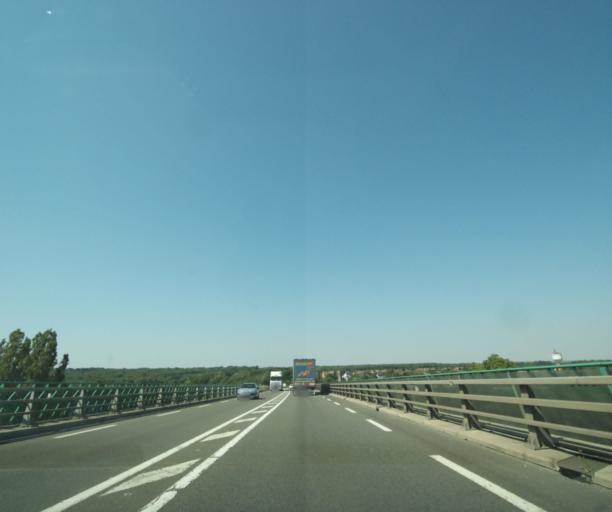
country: FR
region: Lorraine
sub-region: Departement de la Meuse
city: Ancerville
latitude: 48.6258
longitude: 4.9951
